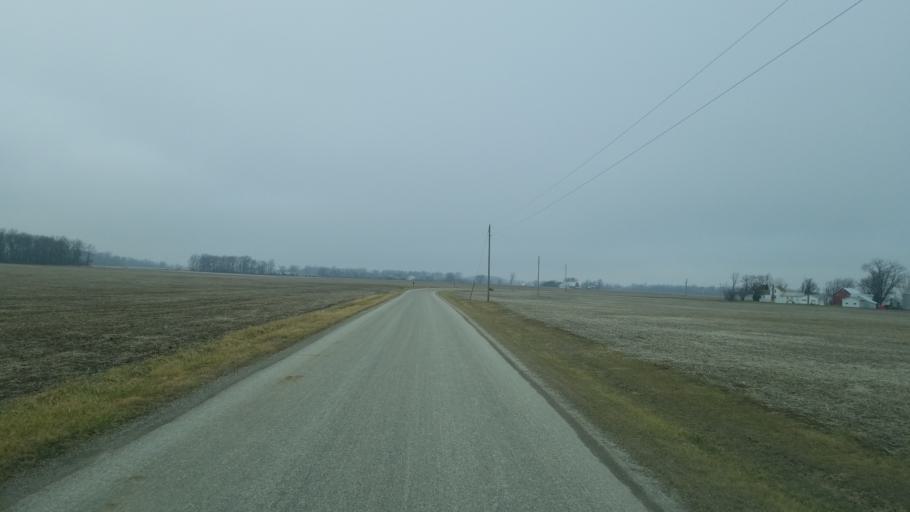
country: US
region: Indiana
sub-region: Adams County
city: Berne
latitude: 40.6799
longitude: -84.8532
